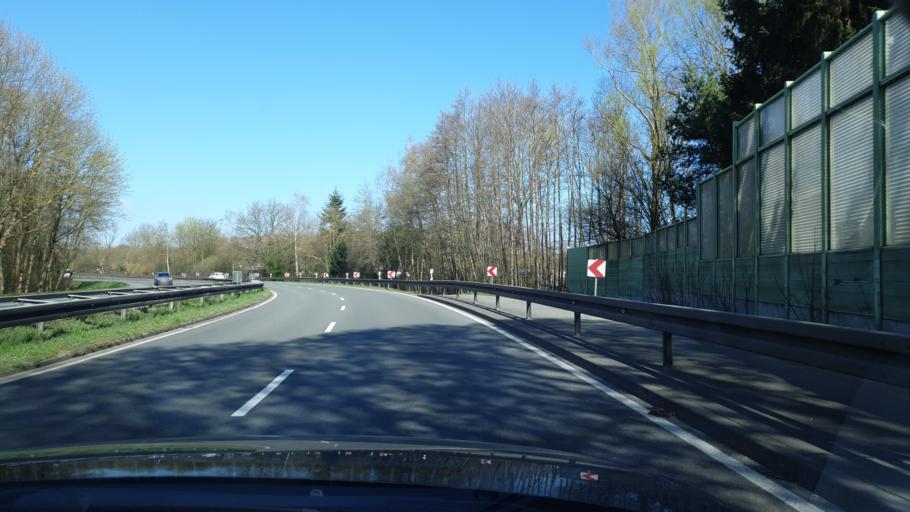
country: DE
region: Mecklenburg-Vorpommern
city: Neumuehle
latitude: 53.6156
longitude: 11.3810
